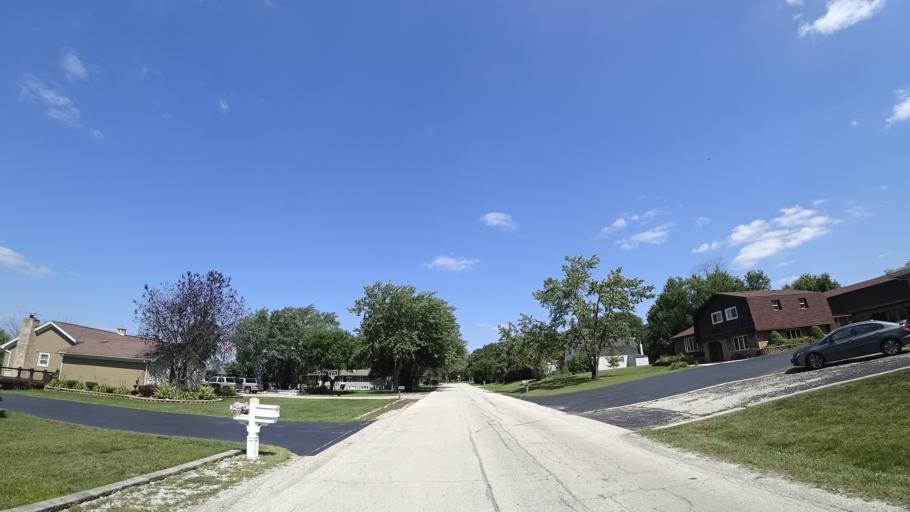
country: US
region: Illinois
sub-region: Cook County
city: Orland Park
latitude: 41.6295
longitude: -87.8456
